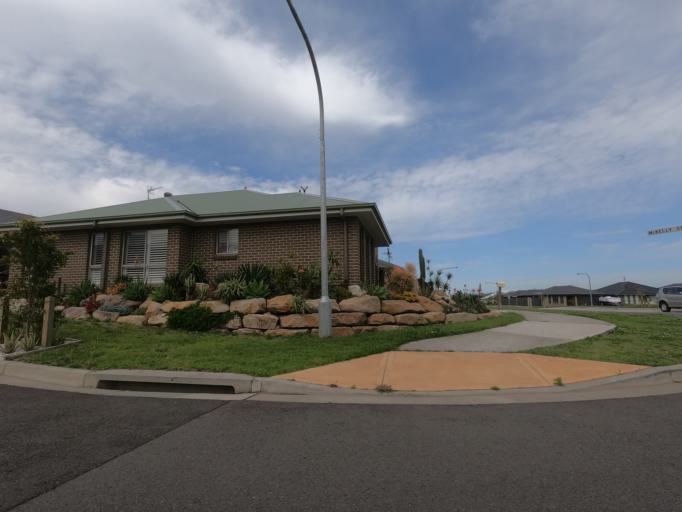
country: AU
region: New South Wales
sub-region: Wollongong
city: Dapto
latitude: -34.4978
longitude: 150.7563
